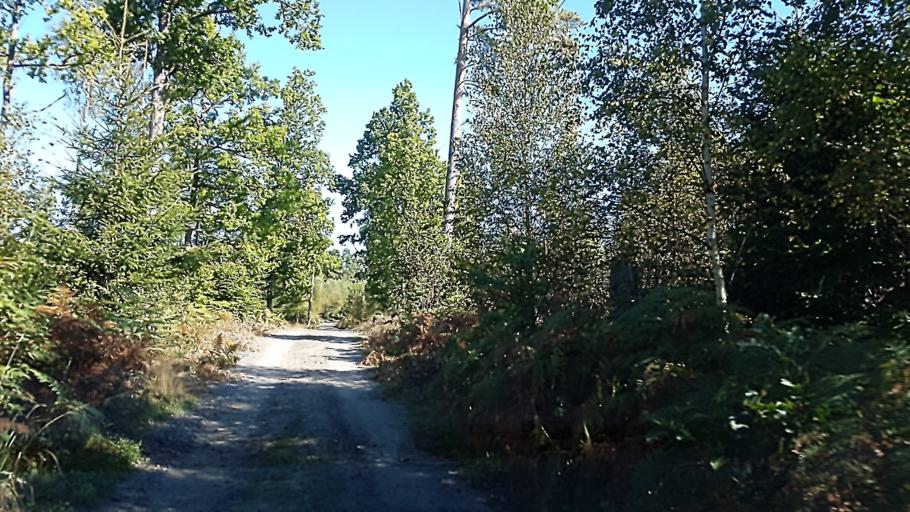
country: SE
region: Kronoberg
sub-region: Ljungby Kommun
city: Ljungby
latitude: 56.8081
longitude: 14.0022
